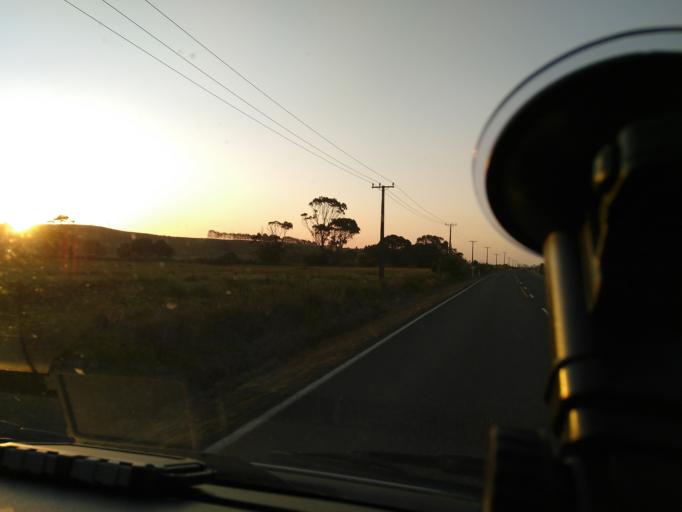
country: NZ
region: Northland
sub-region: Far North District
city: Taipa
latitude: -34.9875
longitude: 173.4128
